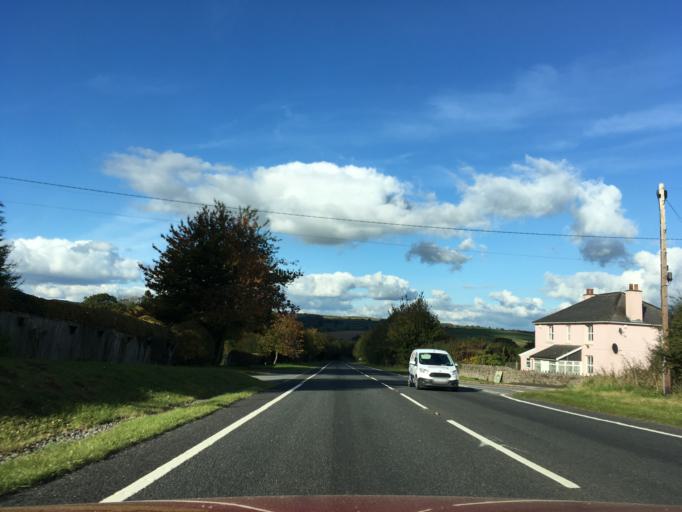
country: GB
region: Wales
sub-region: Sir Powys
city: Brecon
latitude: 51.9805
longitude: -3.3292
